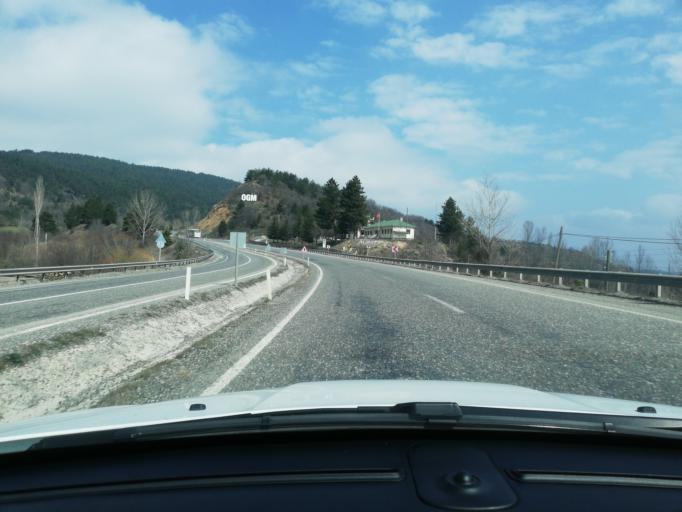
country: TR
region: Kastamonu
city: Kuzyaka
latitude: 41.2026
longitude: 33.7966
